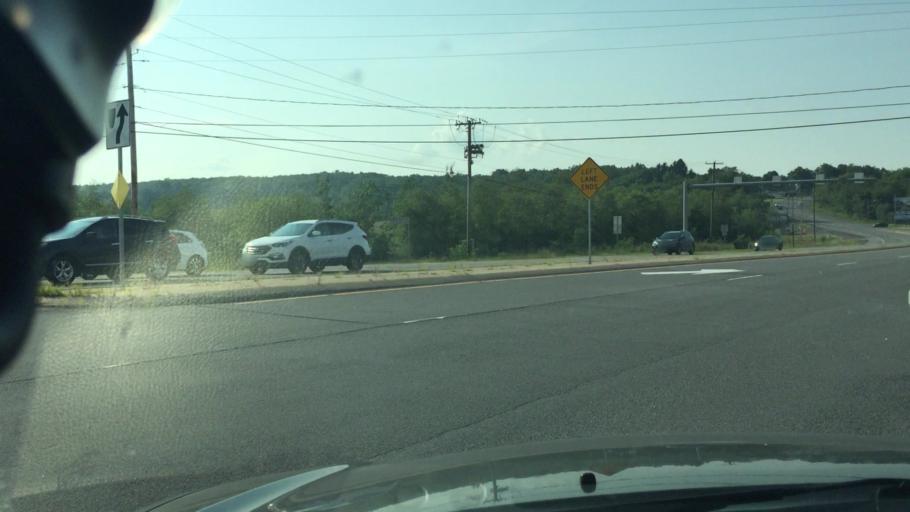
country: US
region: Pennsylvania
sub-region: Luzerne County
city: Harleigh
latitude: 40.9913
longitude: -75.9871
